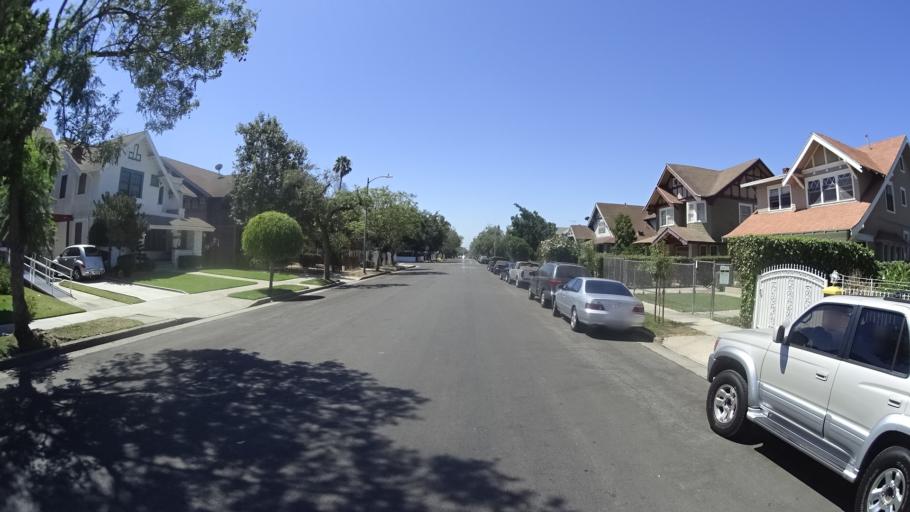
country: US
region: California
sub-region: Los Angeles County
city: Los Angeles
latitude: 34.0299
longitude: -118.2981
